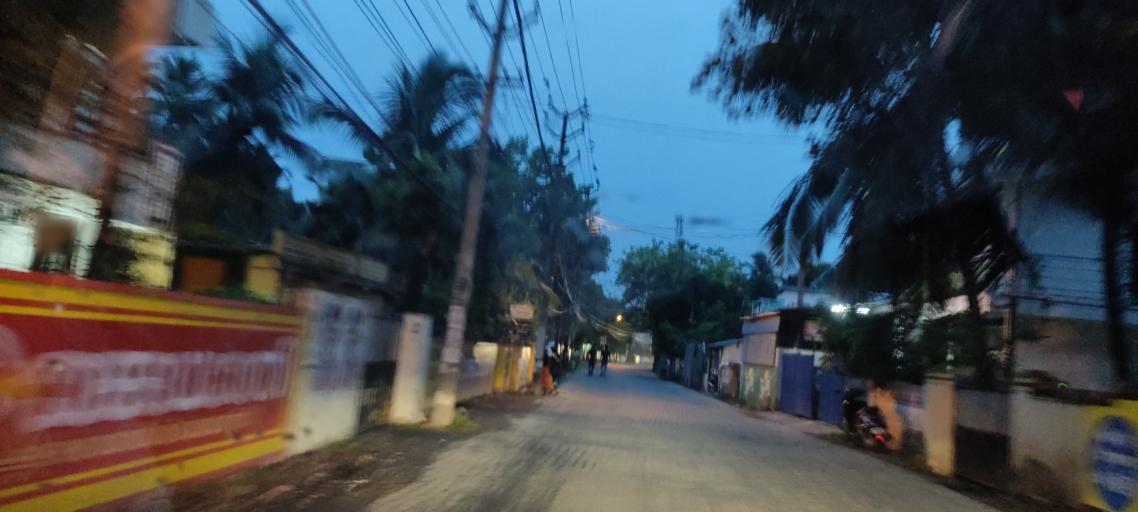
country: IN
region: Kerala
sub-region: Ernakulam
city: Cochin
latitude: 9.9081
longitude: 76.2950
